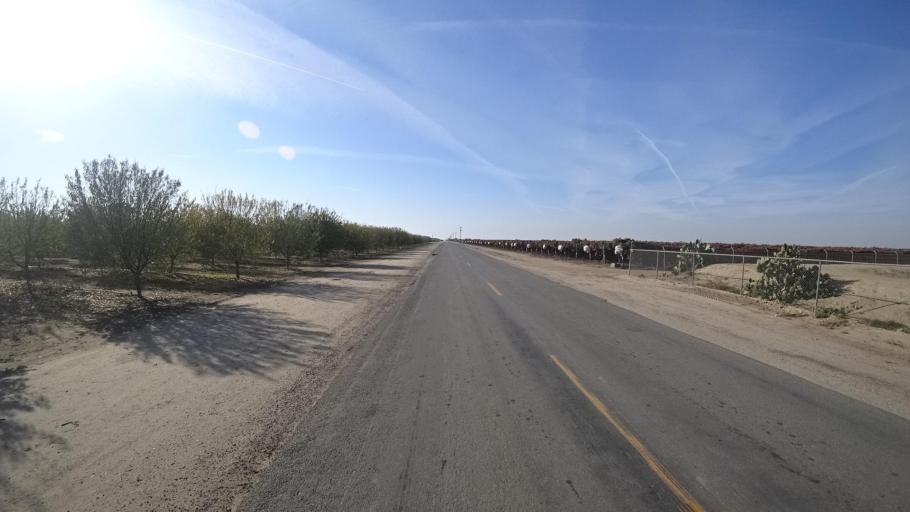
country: US
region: California
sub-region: Kern County
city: McFarland
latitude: 35.7033
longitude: -119.2598
